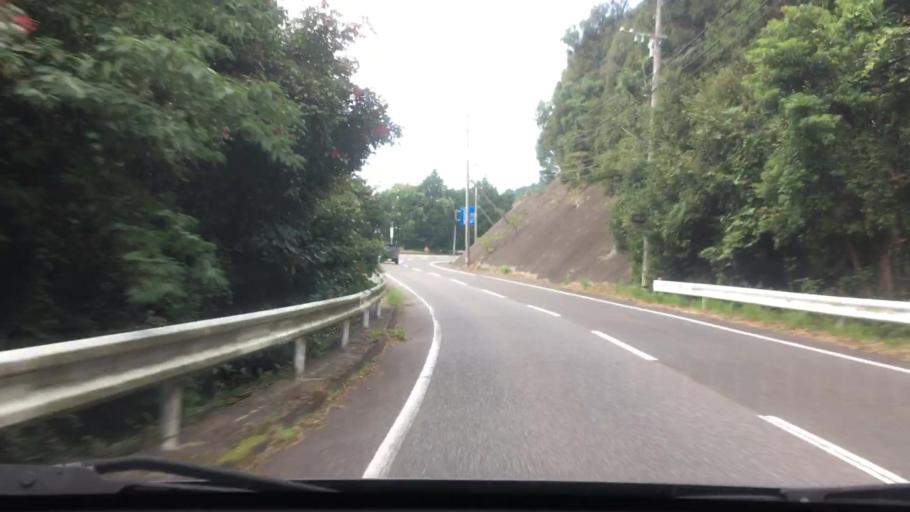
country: JP
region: Nagasaki
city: Sasebo
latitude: 32.9733
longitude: 129.7003
